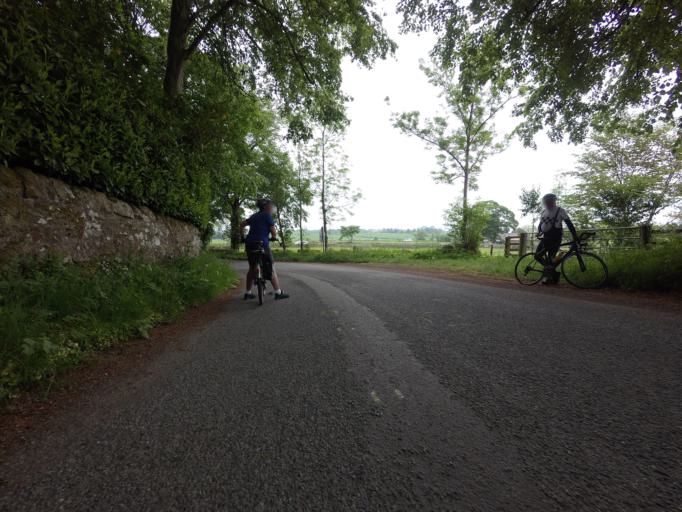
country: GB
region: Scotland
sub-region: Perth and Kinross
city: Kinross
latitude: 56.1639
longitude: -3.4485
